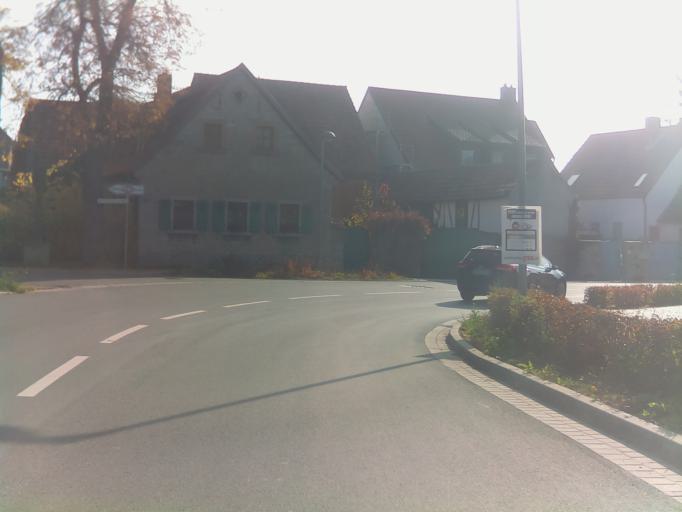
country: DE
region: Bavaria
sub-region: Regierungsbezirk Unterfranken
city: Kleinlangheim
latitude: 49.8156
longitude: 10.2926
